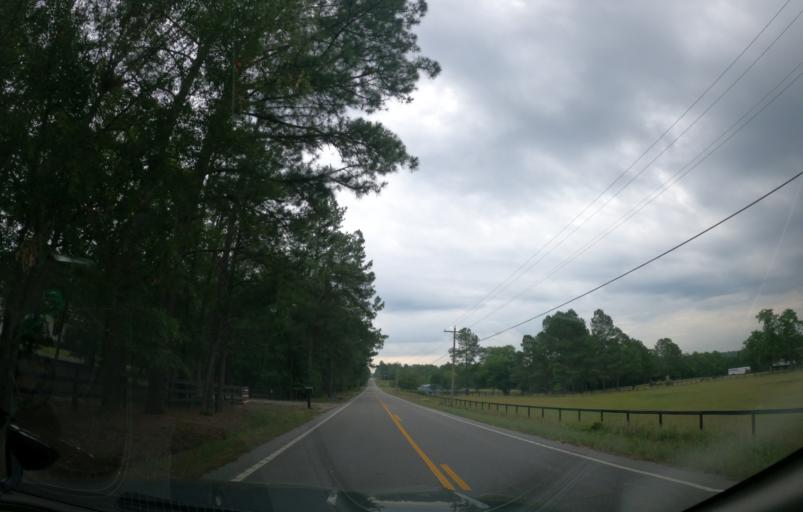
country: US
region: South Carolina
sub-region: Aiken County
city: Aiken
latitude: 33.5713
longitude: -81.6428
